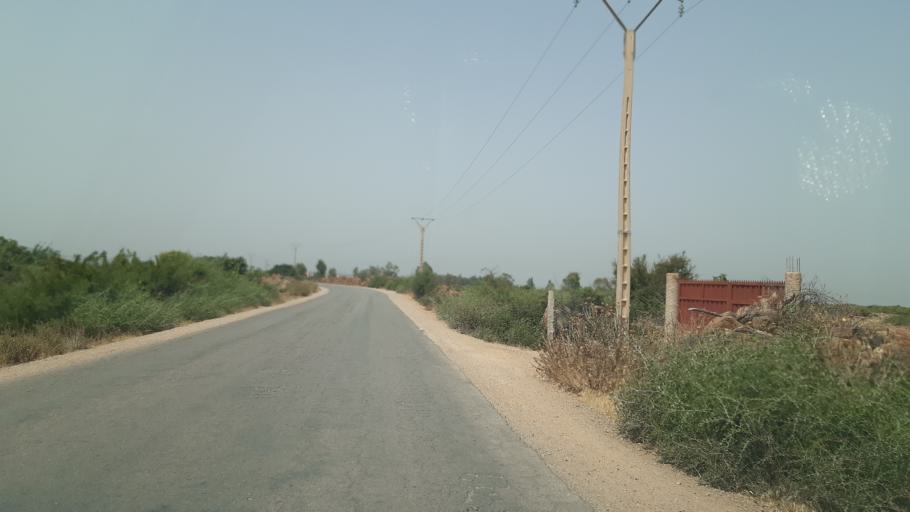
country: MA
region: Fes-Boulemane
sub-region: Fes
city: Oulad Tayeb
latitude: 33.8384
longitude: -5.1327
